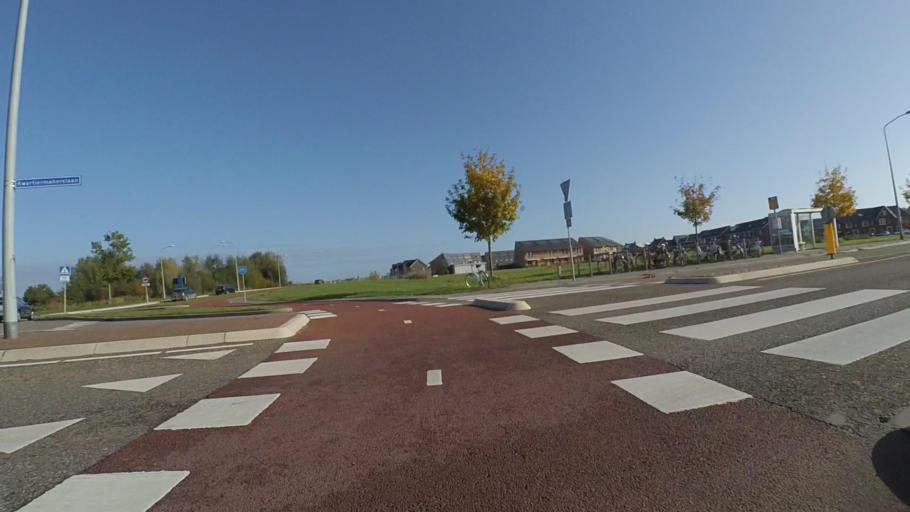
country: NL
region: Flevoland
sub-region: Gemeente Zeewolde
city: Zeewolde
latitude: 52.3435
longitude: 5.5287
